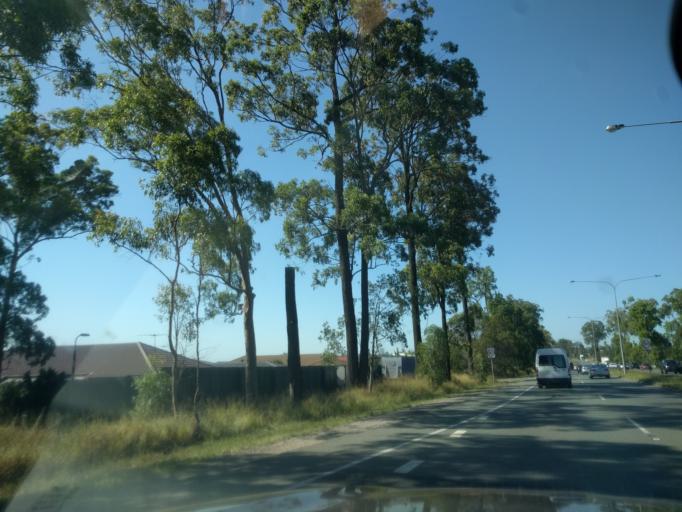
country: AU
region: Queensland
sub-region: Brisbane
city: Sunnybank Hills
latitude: -27.6372
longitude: 153.0449
